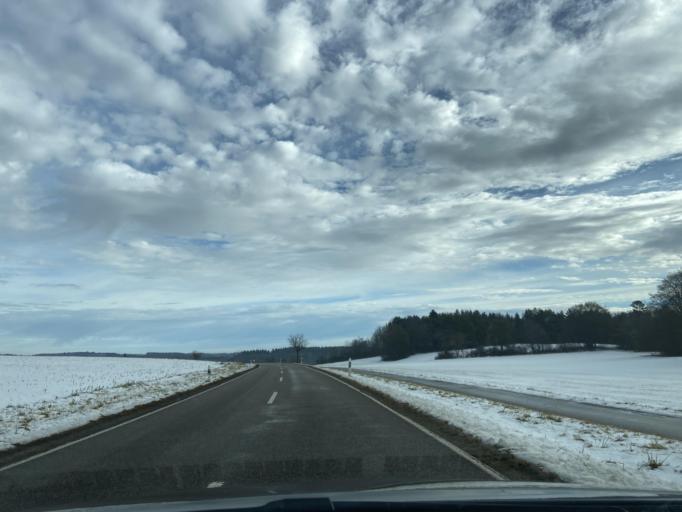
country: DE
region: Baden-Wuerttemberg
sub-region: Tuebingen Region
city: Pfronstetten
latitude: 48.2408
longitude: 9.3217
